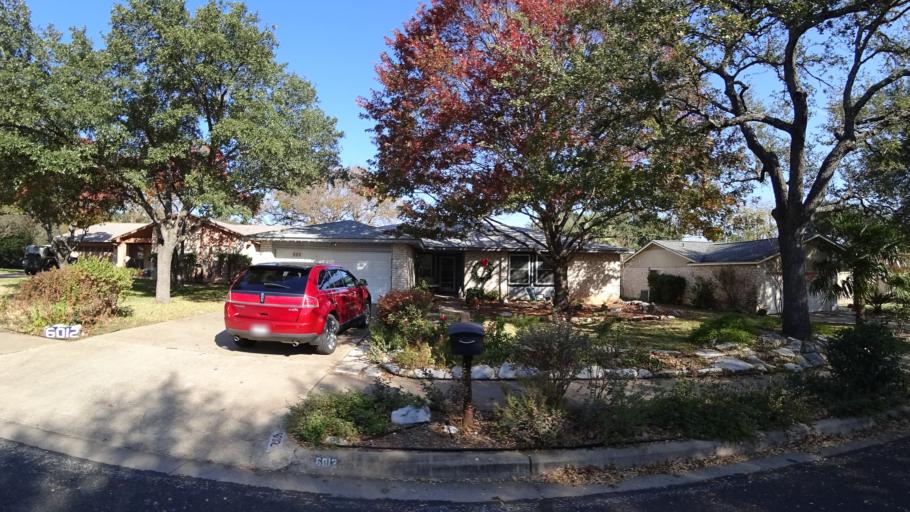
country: US
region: Texas
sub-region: Travis County
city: Barton Creek
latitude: 30.2330
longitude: -97.8474
